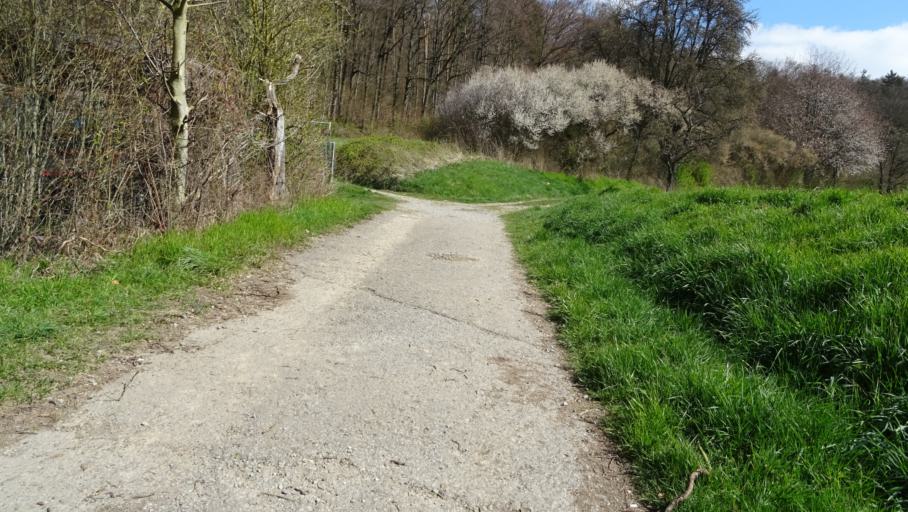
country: DE
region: Baden-Wuerttemberg
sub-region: Karlsruhe Region
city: Neckarzimmern
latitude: 49.3319
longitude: 9.1207
